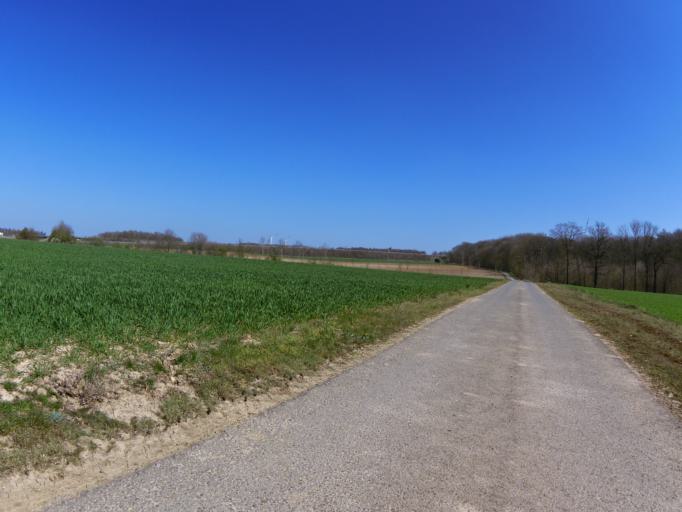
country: DE
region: Bavaria
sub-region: Regierungsbezirk Unterfranken
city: Biebelried
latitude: 49.7751
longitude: 10.0857
